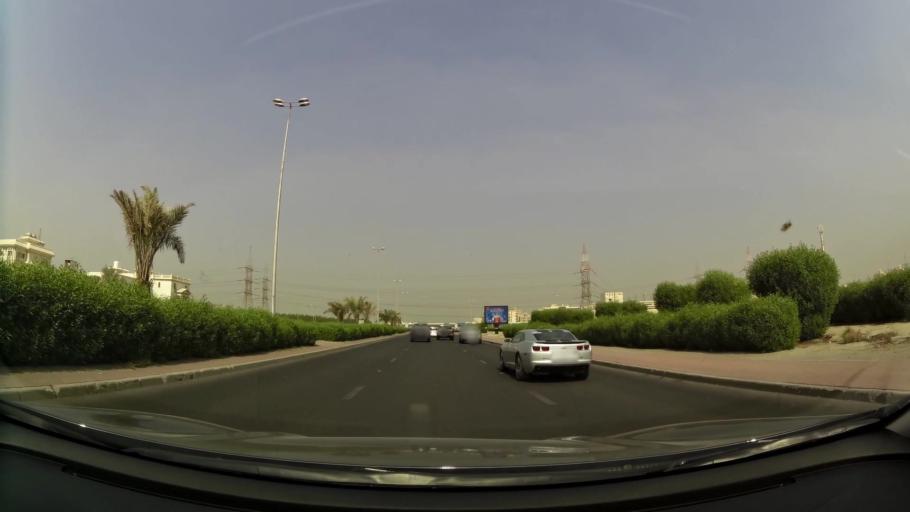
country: KW
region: Al Asimah
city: Ar Rabiyah
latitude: 29.2950
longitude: 47.9059
